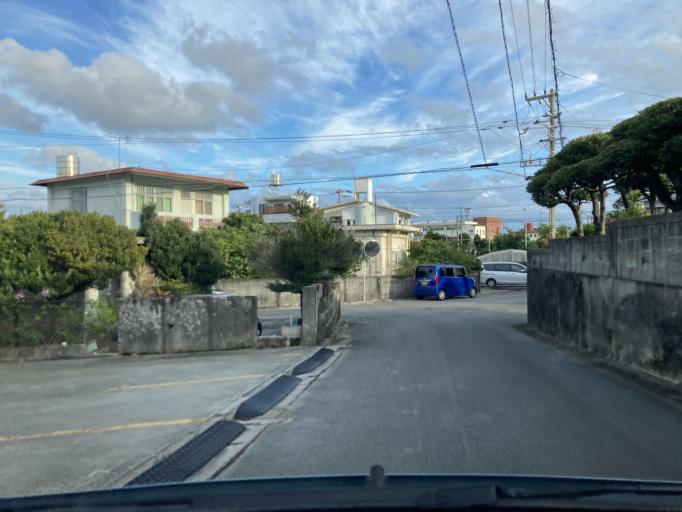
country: JP
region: Okinawa
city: Itoman
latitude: 26.1338
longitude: 127.7259
